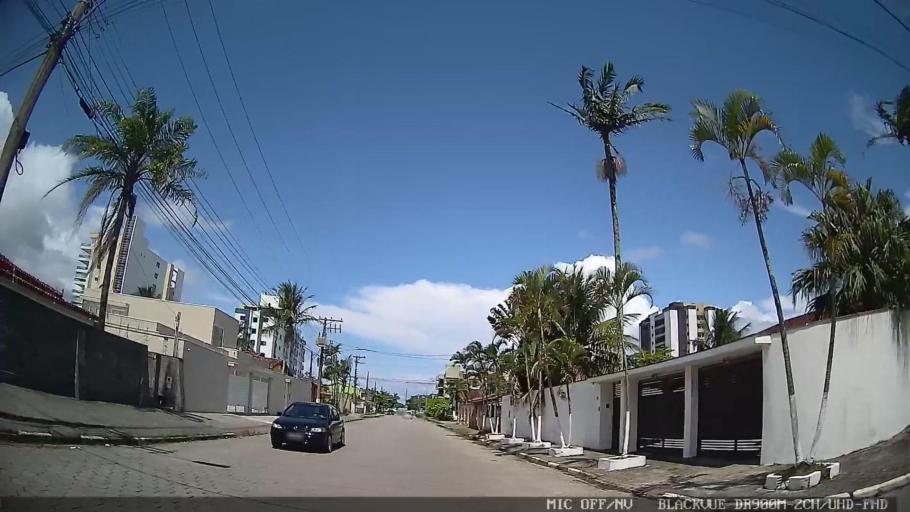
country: BR
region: Sao Paulo
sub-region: Caraguatatuba
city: Caraguatatuba
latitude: -23.6420
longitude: -45.4259
